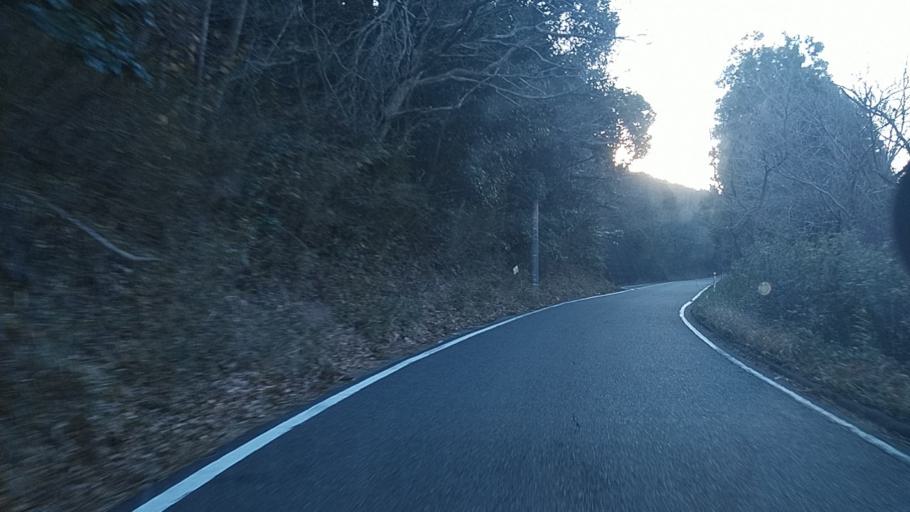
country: JP
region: Chiba
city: Kimitsu
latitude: 35.2601
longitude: 139.9442
